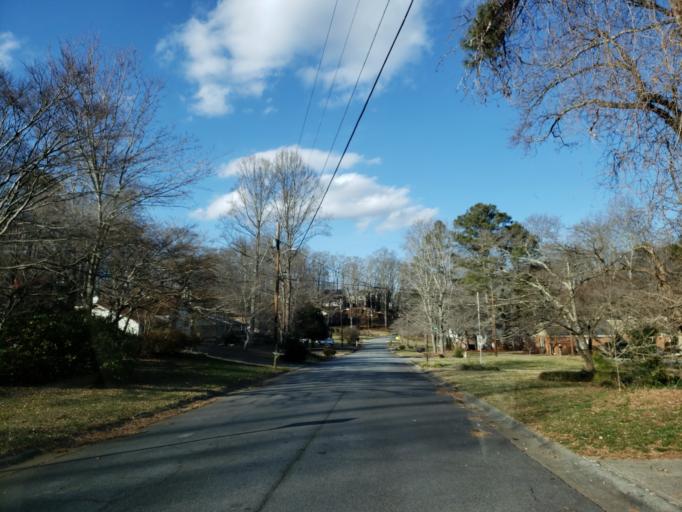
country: US
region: Georgia
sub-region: Cherokee County
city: Woodstock
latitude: 34.0322
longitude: -84.4891
